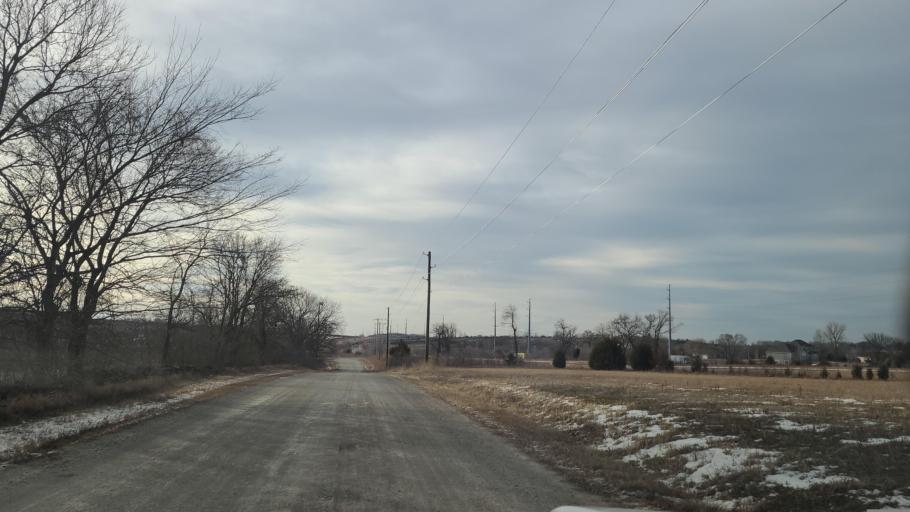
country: US
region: Kansas
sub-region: Douglas County
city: Lawrence
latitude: 38.9837
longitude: -95.3352
